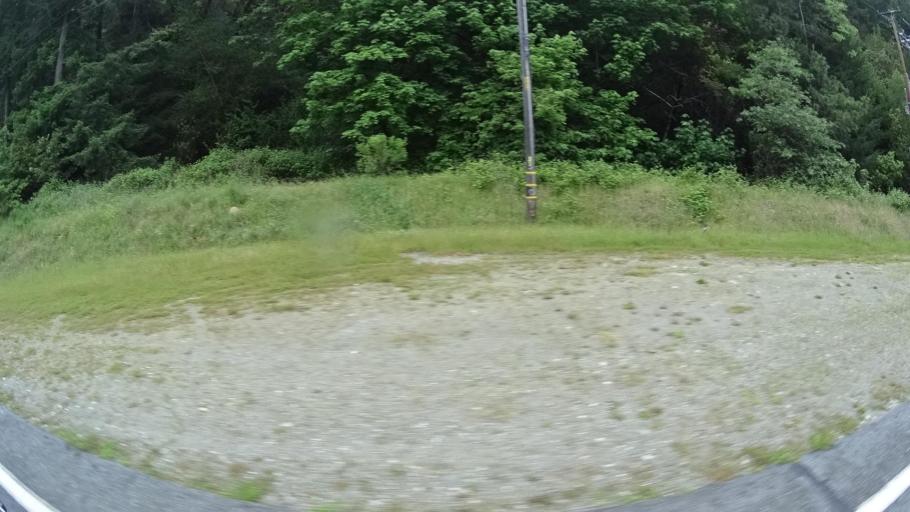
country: US
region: California
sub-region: Humboldt County
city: Willow Creek
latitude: 41.2525
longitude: -123.6365
